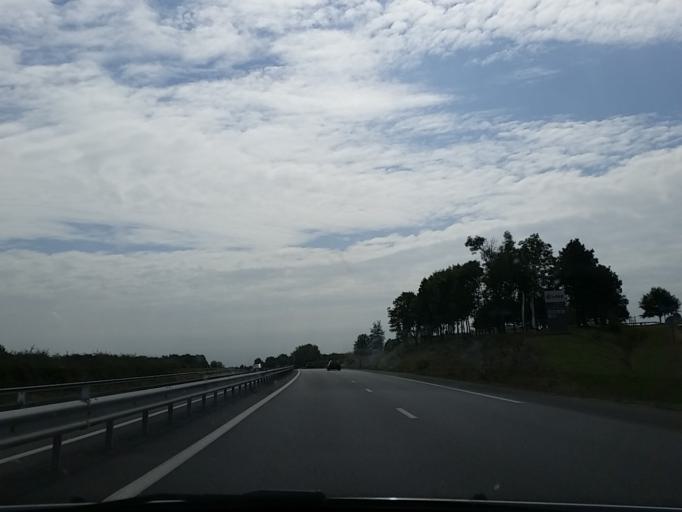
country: FR
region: Auvergne
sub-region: Departement de l'Allier
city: Vallon-en-Sully
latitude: 46.5170
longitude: 2.5805
